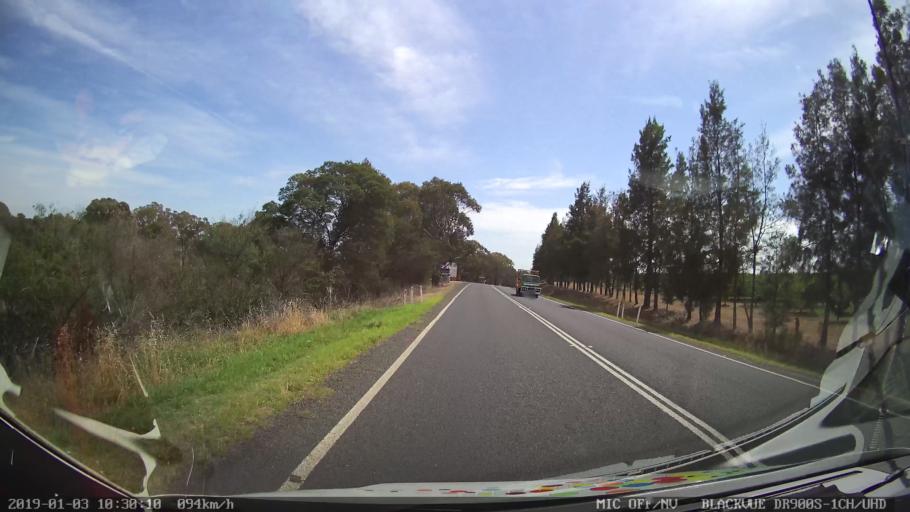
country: AU
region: New South Wales
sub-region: Young
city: Young
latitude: -34.3650
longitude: 148.2650
